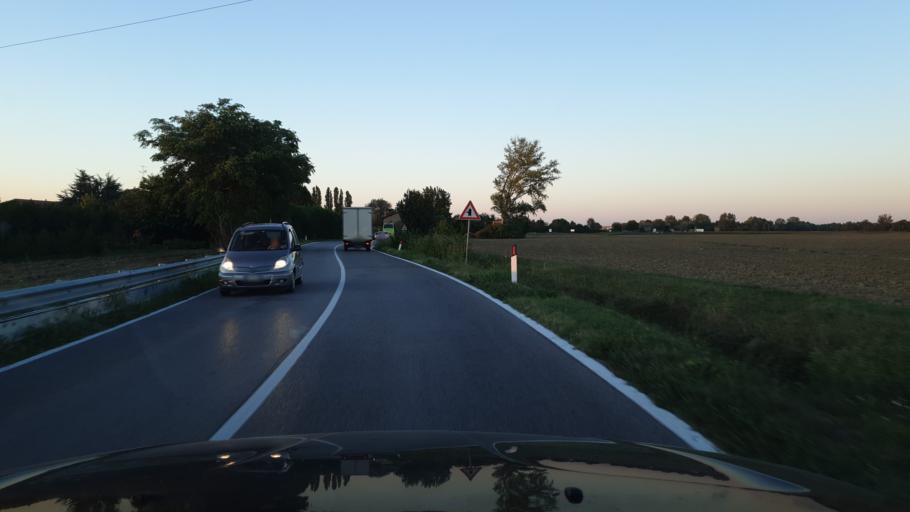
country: IT
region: Emilia-Romagna
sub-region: Provincia di Bologna
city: Progresso
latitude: 44.5702
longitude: 11.4043
